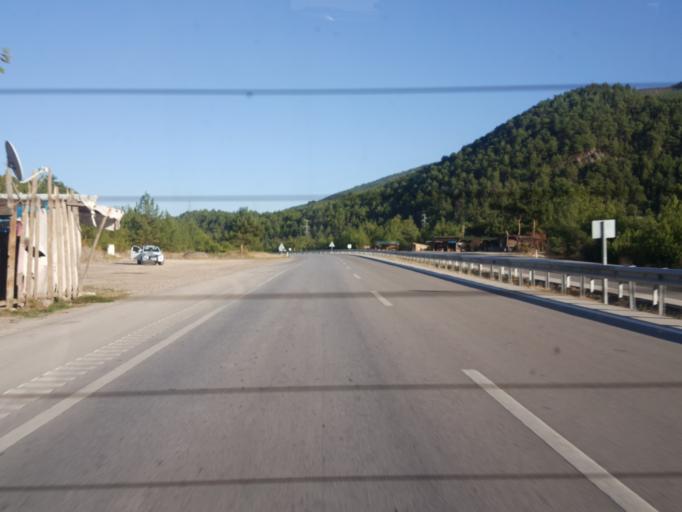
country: TR
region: Amasya
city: Akdag
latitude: 40.7527
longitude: 36.0741
